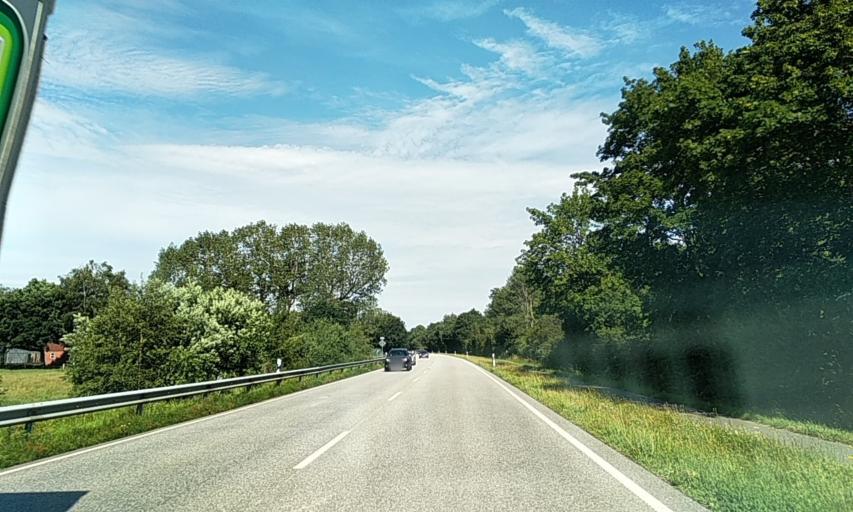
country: DE
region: Schleswig-Holstein
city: Fockbek
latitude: 54.3373
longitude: 9.6116
